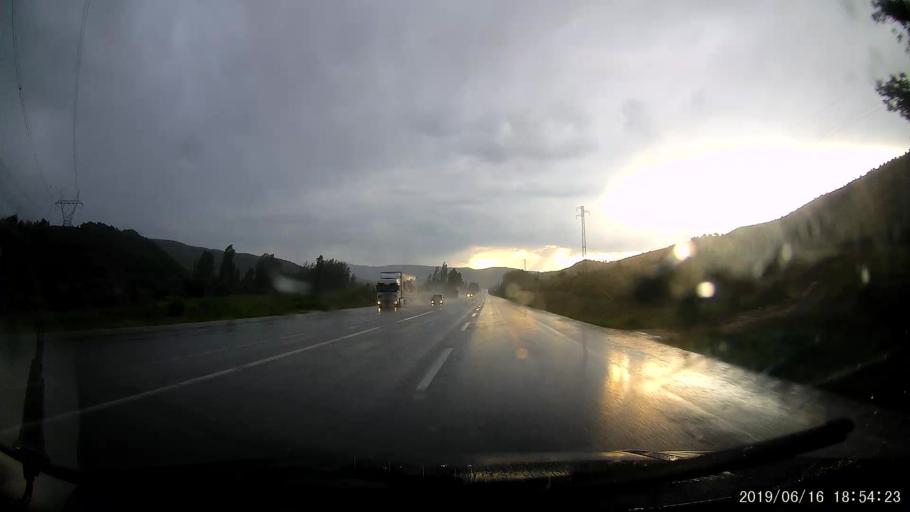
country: TR
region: Erzincan
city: Catalcam
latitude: 39.8968
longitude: 38.8549
